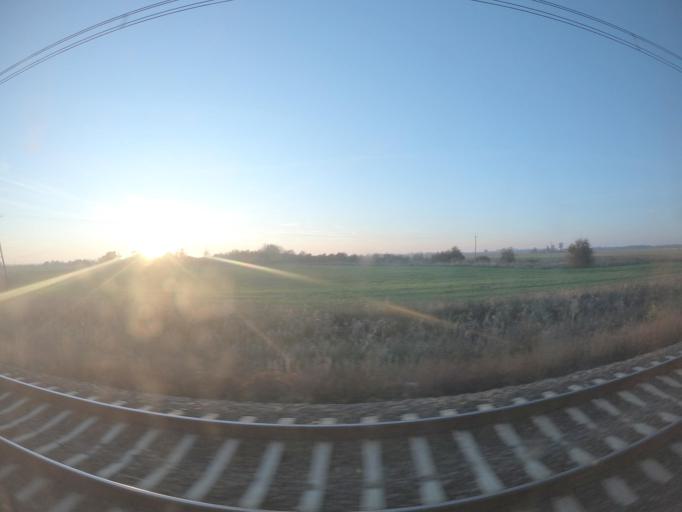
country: PL
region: Lubusz
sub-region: Powiat gorzowski
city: Kostrzyn nad Odra
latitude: 52.5437
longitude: 14.6509
